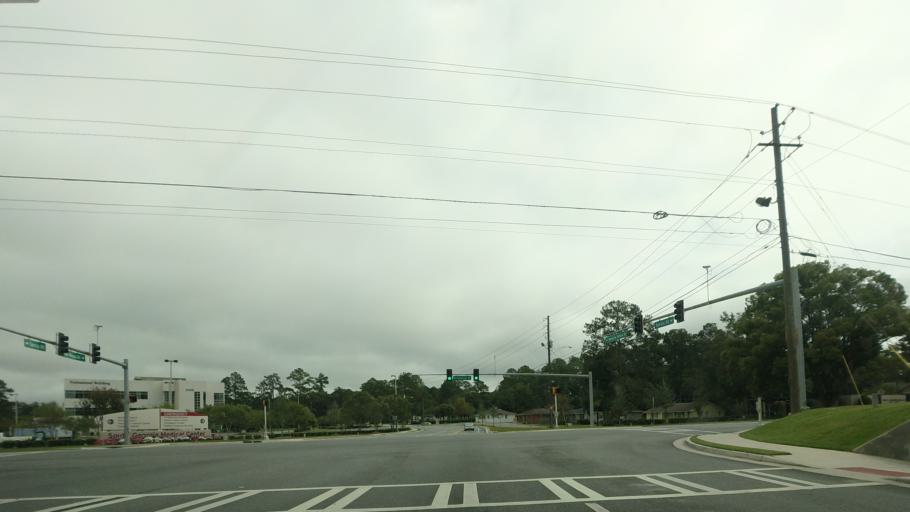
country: US
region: Georgia
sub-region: Lowndes County
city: Remerton
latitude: 30.8597
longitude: -83.2892
